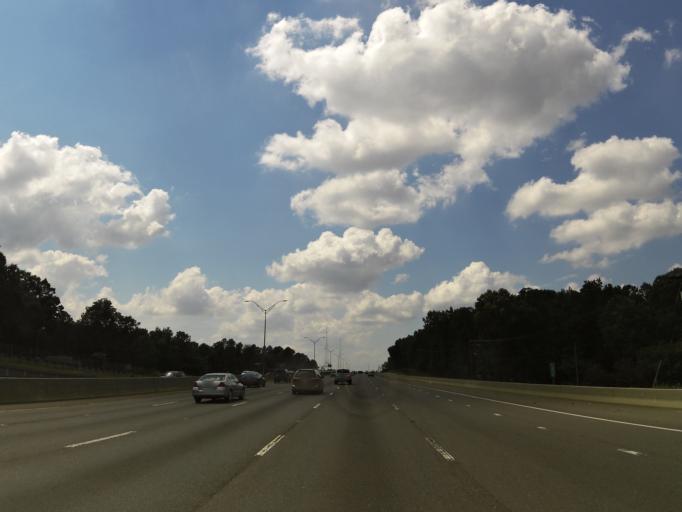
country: US
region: North Carolina
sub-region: Mecklenburg County
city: Charlotte
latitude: 35.2818
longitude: -80.7830
